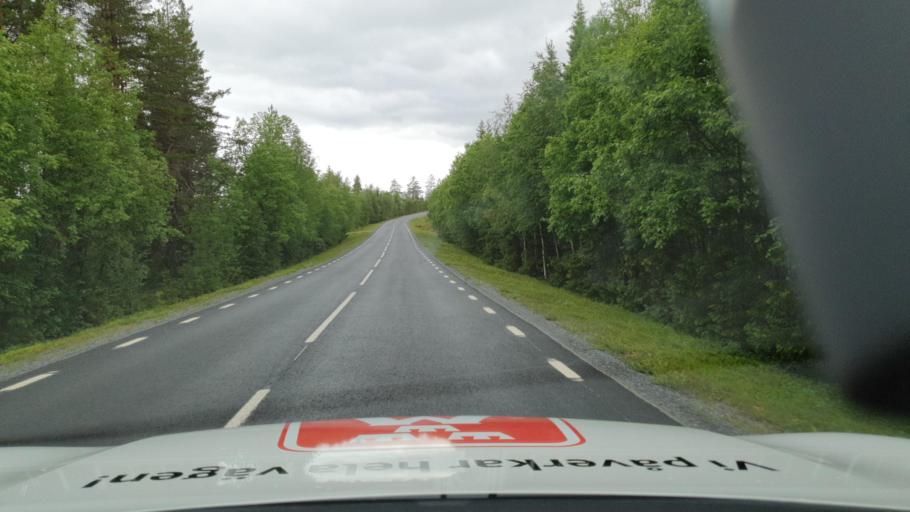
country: SE
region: Vaesterbotten
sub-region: Dorotea Kommun
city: Dorotea
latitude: 64.2025
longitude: 16.5672
